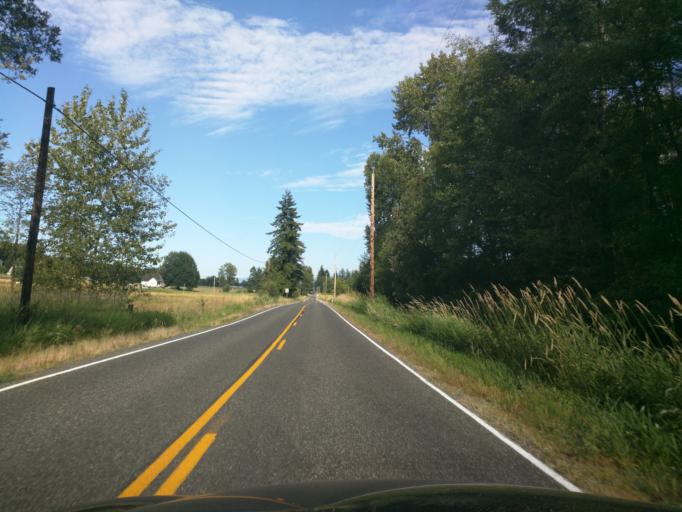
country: CA
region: British Columbia
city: Langley
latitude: 48.9933
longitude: -122.5556
